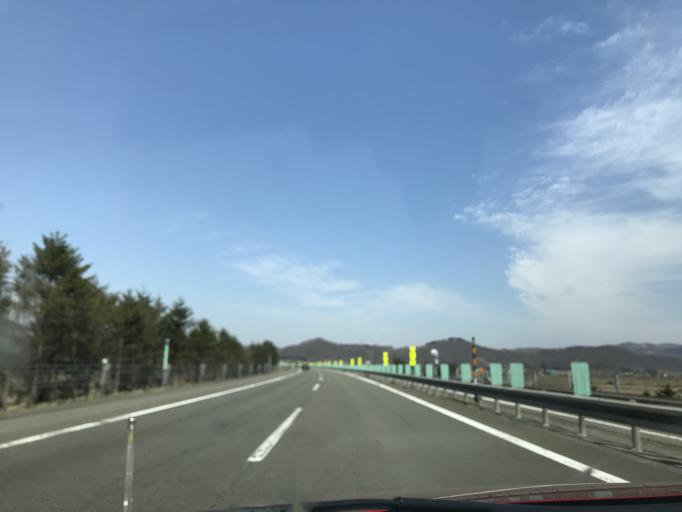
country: JP
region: Hokkaido
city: Iwamizawa
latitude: 43.2262
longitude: 141.8302
